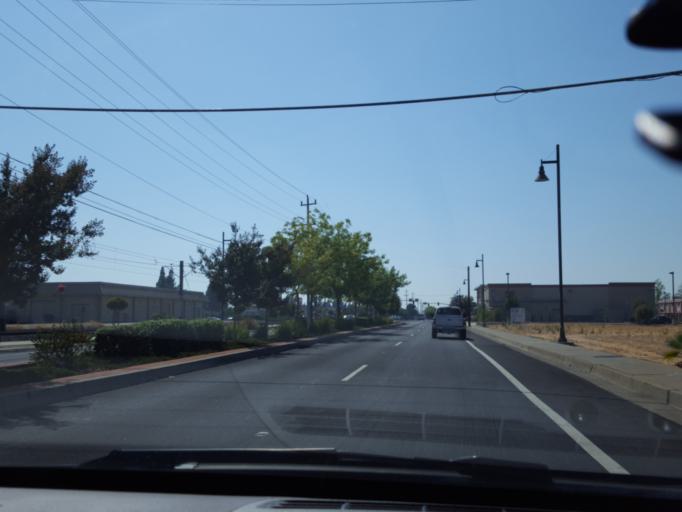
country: US
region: California
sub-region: Sacramento County
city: Rancho Cordova
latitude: 38.5976
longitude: -121.2858
